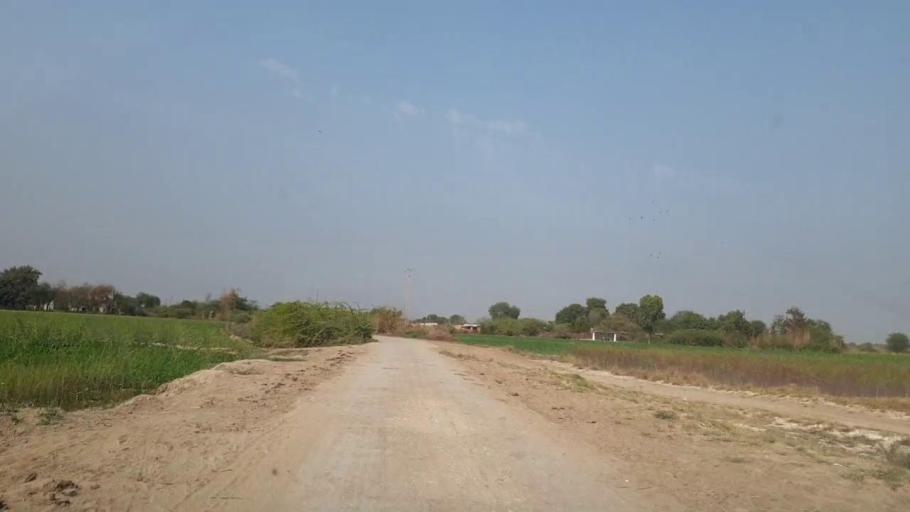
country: PK
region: Sindh
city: Mirpur Khas
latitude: 25.5700
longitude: 69.1522
